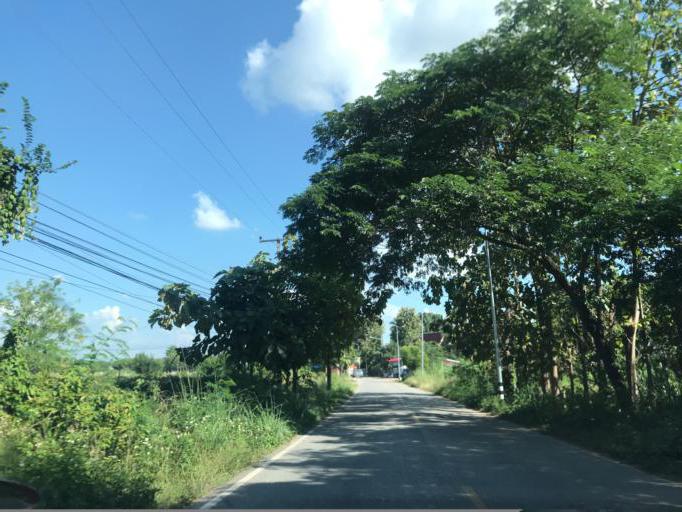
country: TH
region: Lamphun
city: Pa Sang
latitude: 18.5299
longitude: 98.8459
